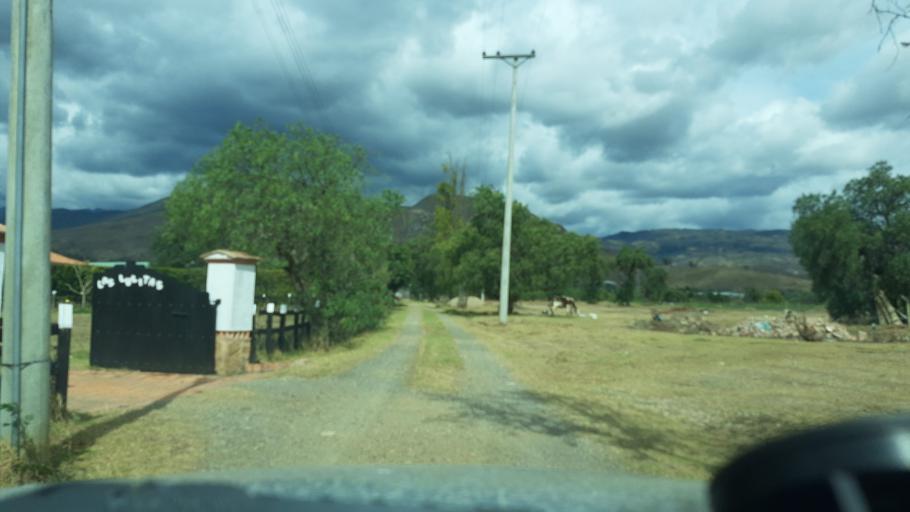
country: CO
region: Boyaca
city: Sachica
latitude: 5.5929
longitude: -73.5452
